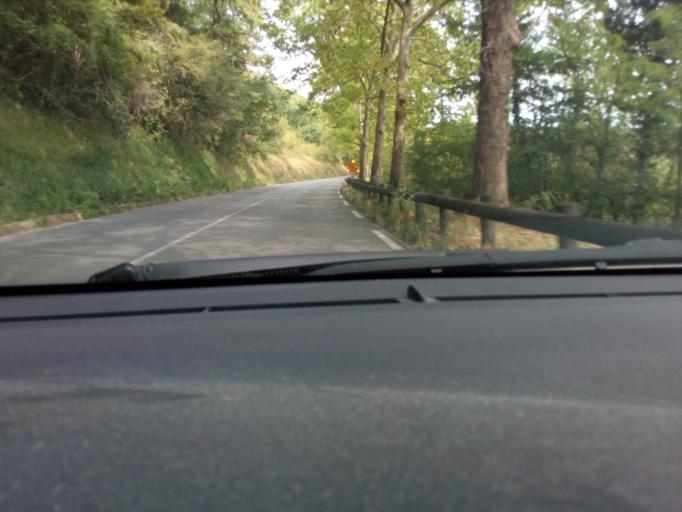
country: FR
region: Poitou-Charentes
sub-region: Departement de la Charente
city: Fleac
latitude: 45.6733
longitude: 0.1060
